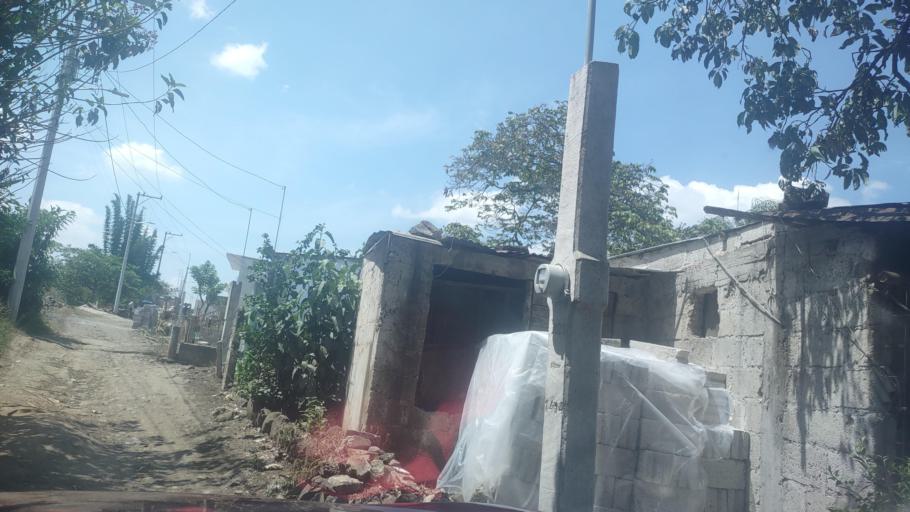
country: MX
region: Veracruz
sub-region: Coatepec
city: Las Lomas
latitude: 19.4081
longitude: -96.9142
